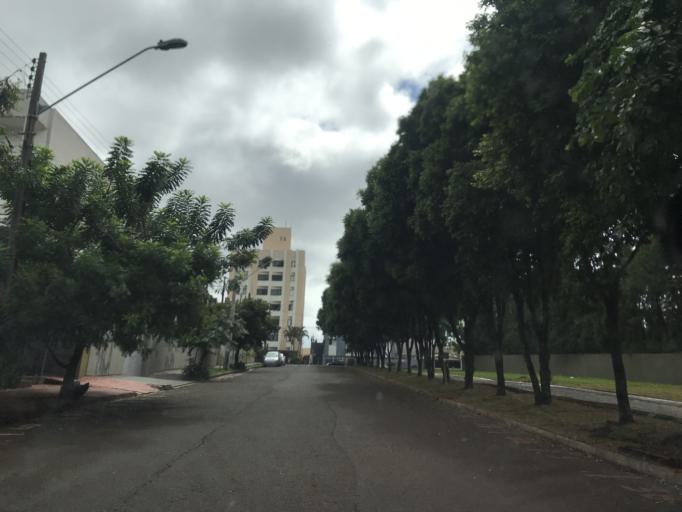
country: BR
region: Parana
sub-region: Londrina
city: Londrina
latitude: -23.3239
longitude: -51.1702
